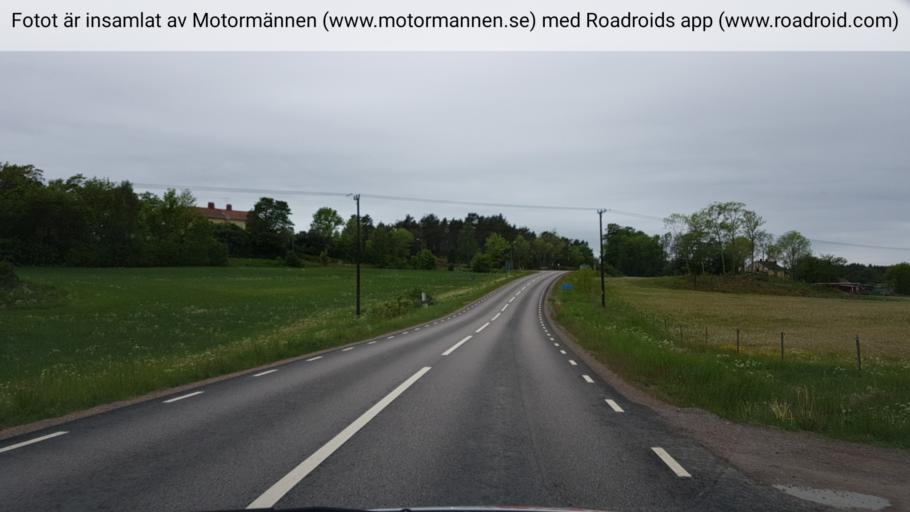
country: SE
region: Kalmar
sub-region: Vasterviks Kommun
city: Forserum
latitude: 57.9378
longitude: 16.4662
